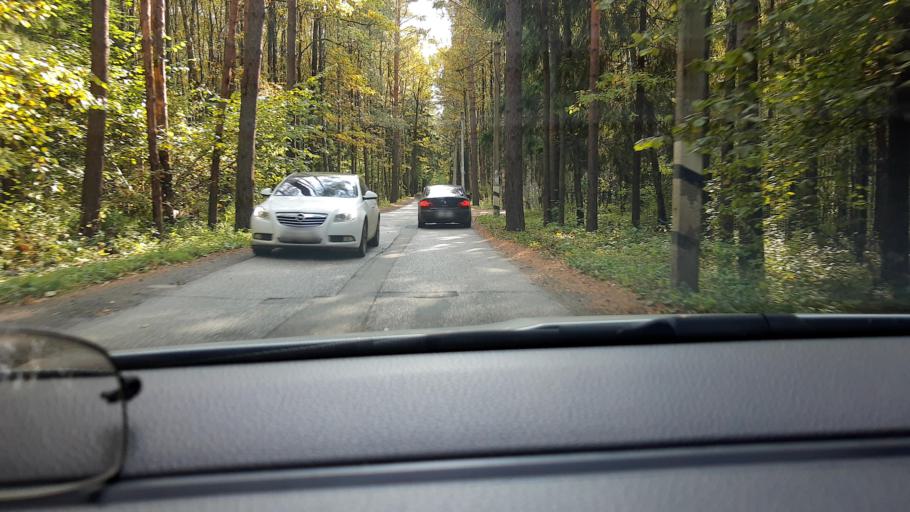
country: RU
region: Moskovskaya
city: Barvikha
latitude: 55.7192
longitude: 37.3037
